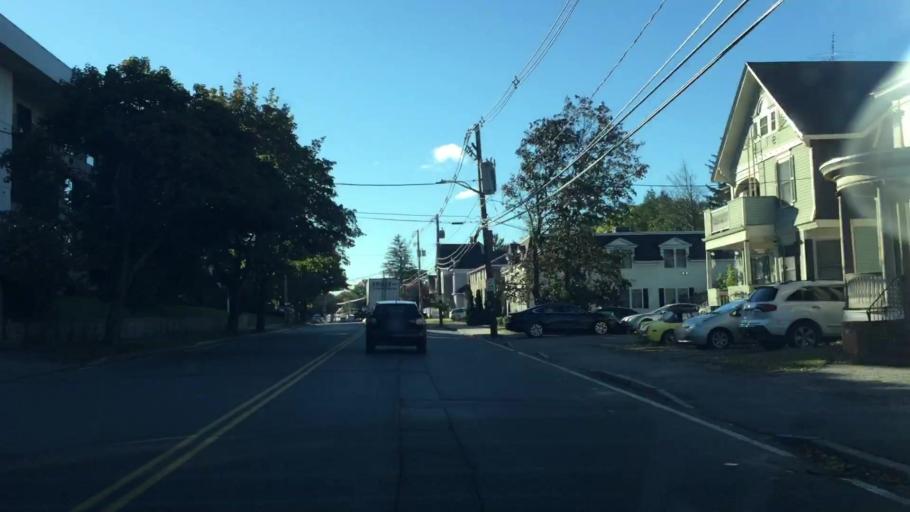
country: US
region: Massachusetts
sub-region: Middlesex County
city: Lowell
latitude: 42.6401
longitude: -71.2961
